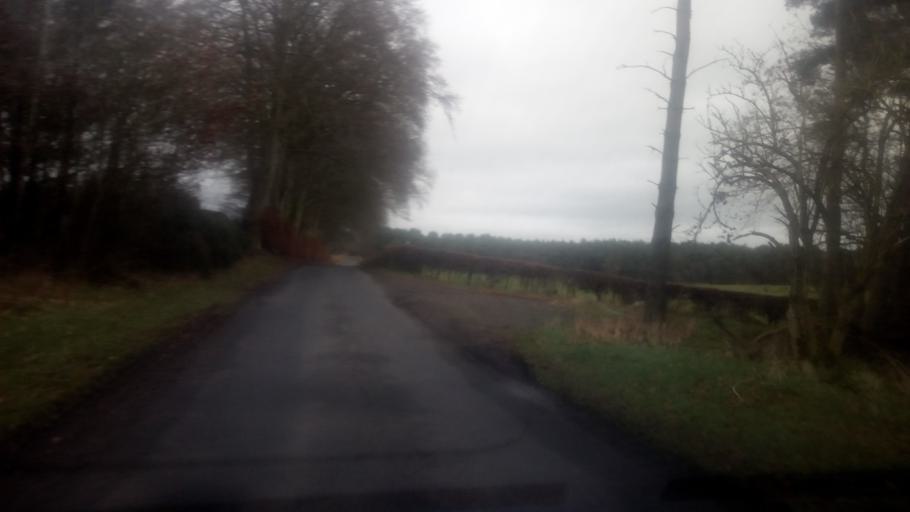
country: GB
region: Scotland
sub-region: The Scottish Borders
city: Jedburgh
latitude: 55.5396
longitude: -2.4954
